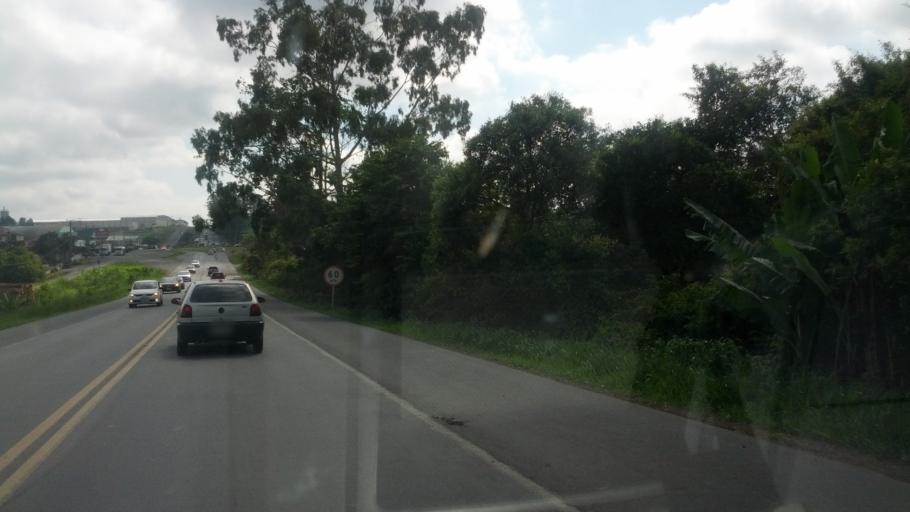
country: BR
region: Santa Catarina
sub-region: Rio Do Sul
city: Rio do Sul
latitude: -27.2595
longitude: -49.9178
